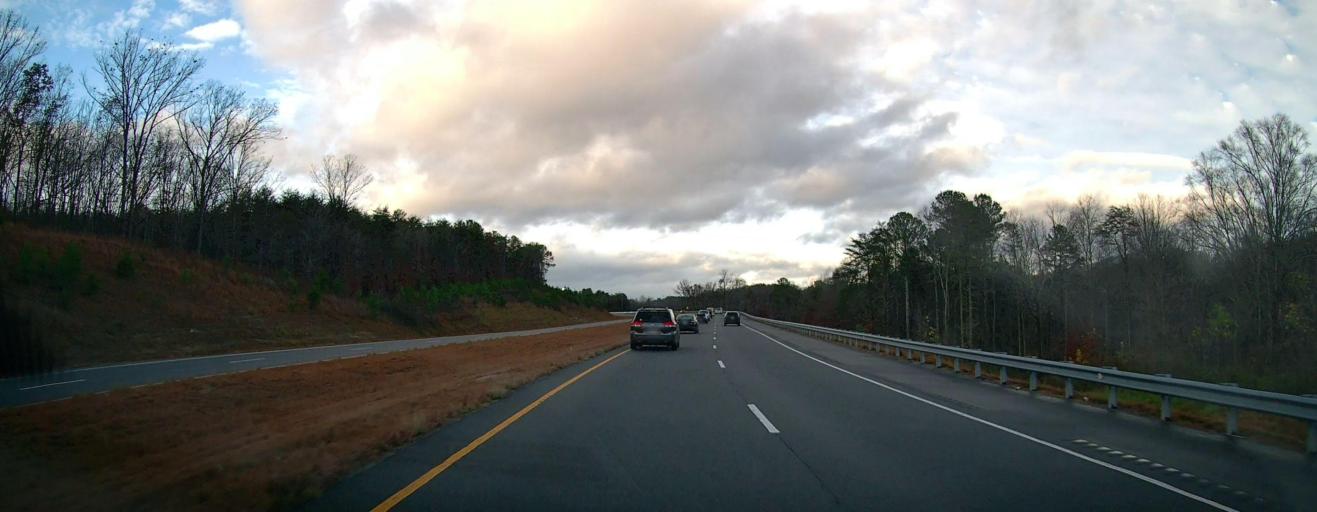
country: US
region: Georgia
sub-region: White County
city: Cleveland
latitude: 34.5950
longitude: -83.7821
